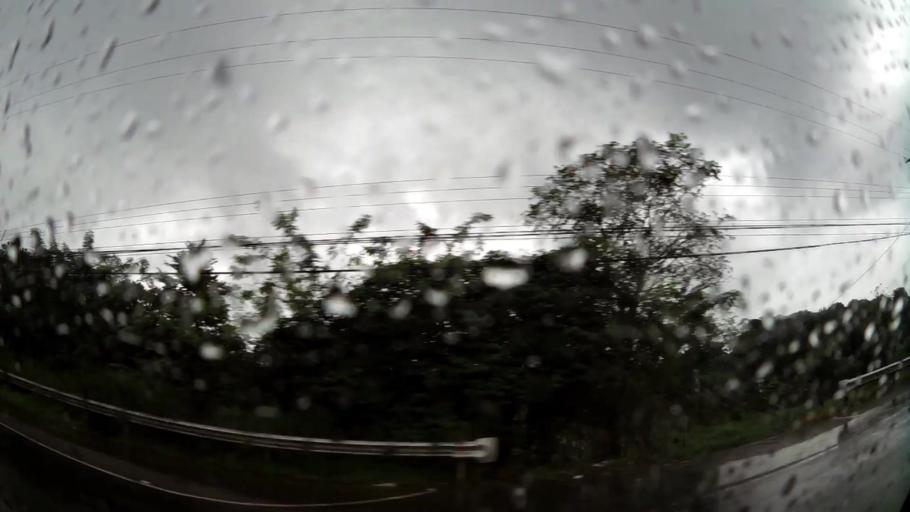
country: PA
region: Colon
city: Buena Vista
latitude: 9.2757
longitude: -79.6989
